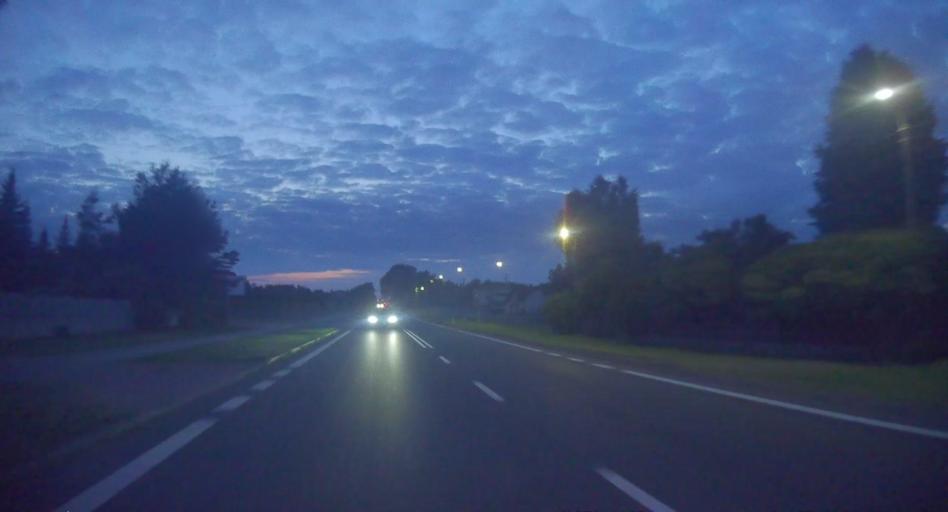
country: PL
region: Silesian Voivodeship
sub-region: Powiat klobucki
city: Kamyk
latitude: 50.8686
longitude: 19.0122
